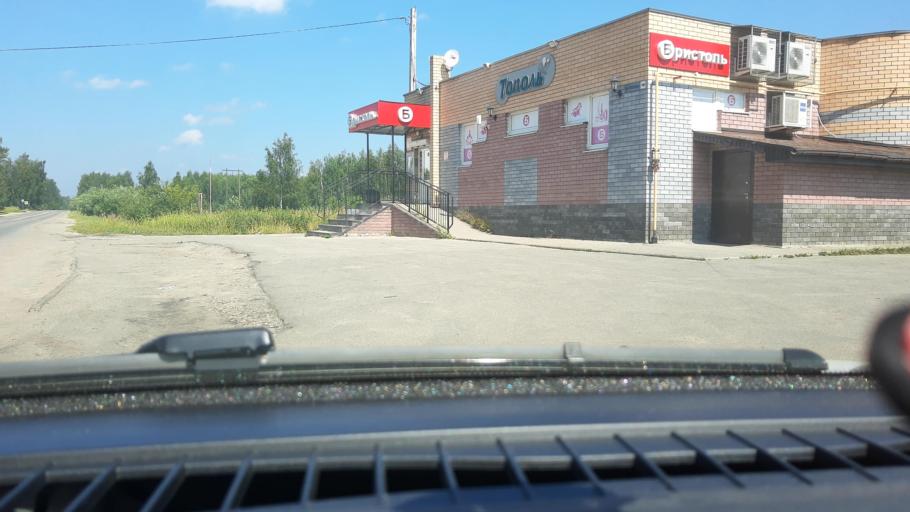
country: RU
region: Nizjnij Novgorod
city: Afonino
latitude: 56.3032
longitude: 44.1839
